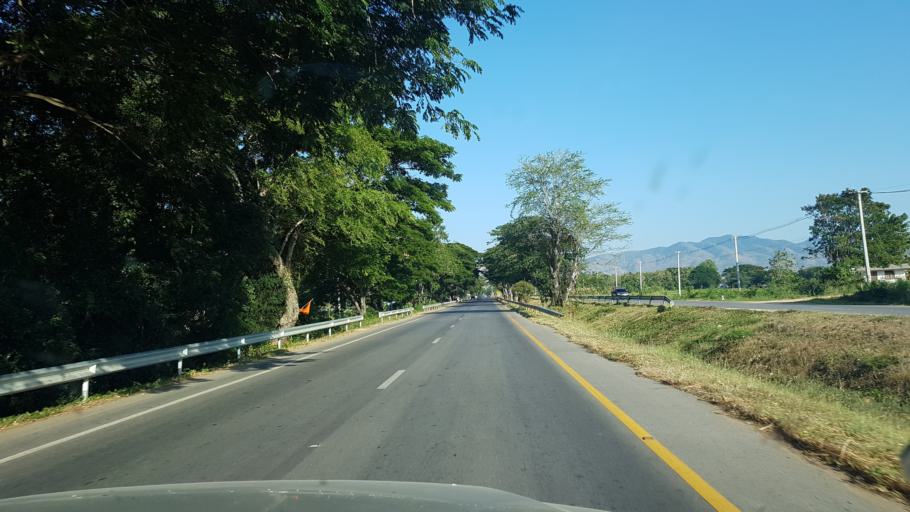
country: TH
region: Phetchabun
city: Lom Sak
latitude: 16.7275
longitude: 101.2662
